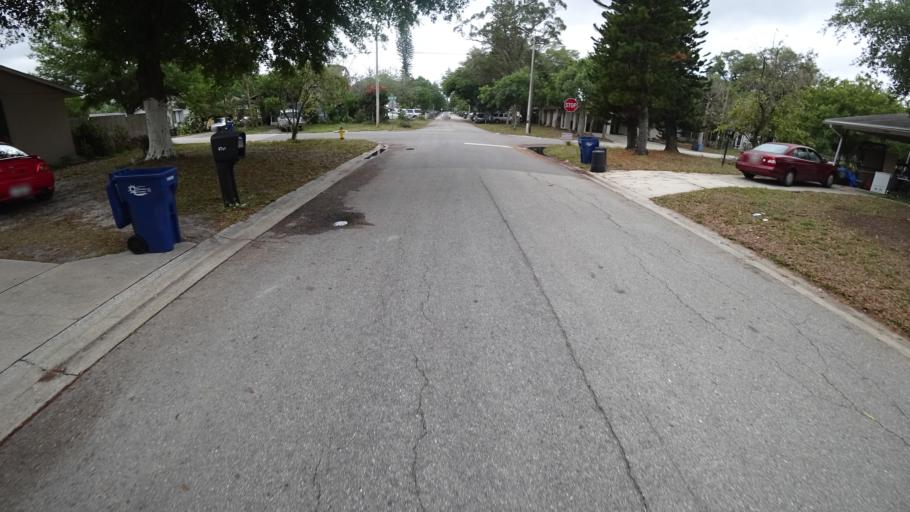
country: US
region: Florida
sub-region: Manatee County
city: South Bradenton
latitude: 27.4564
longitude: -82.5799
